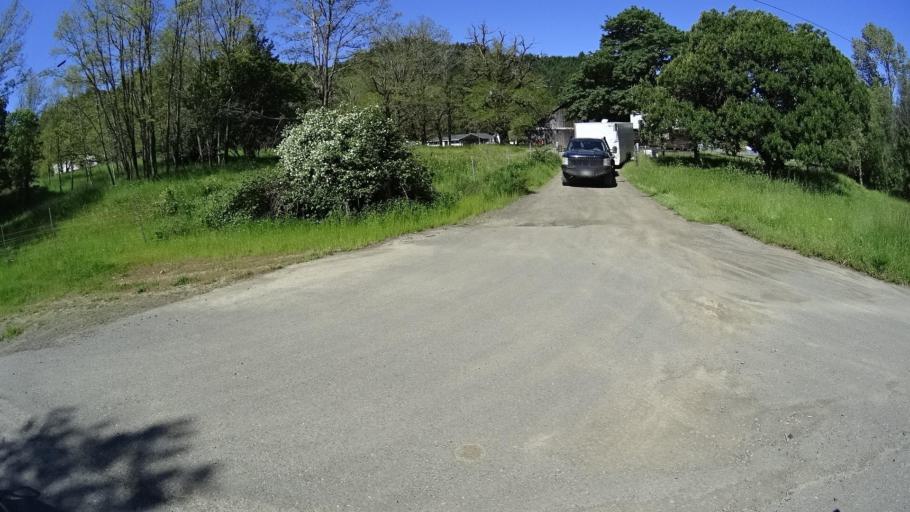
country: US
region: California
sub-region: Humboldt County
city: Rio Dell
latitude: 40.2336
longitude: -124.1163
